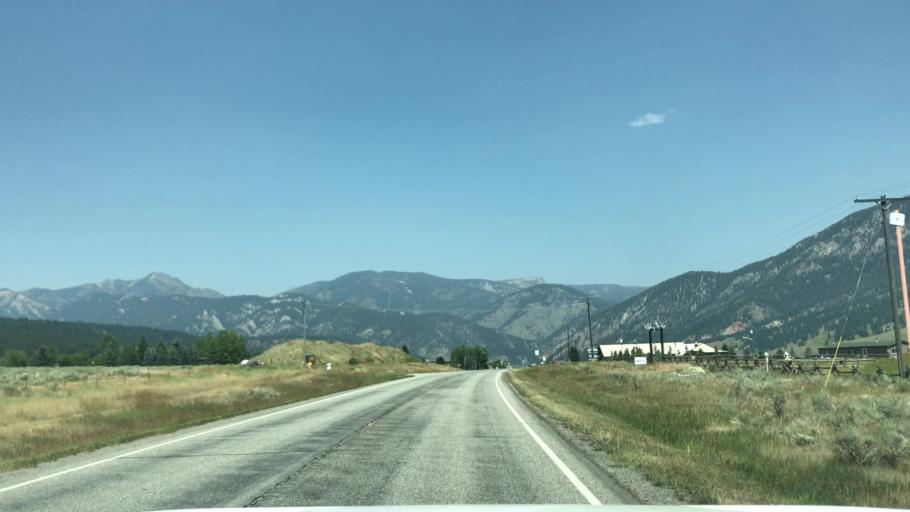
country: US
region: Montana
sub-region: Gallatin County
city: Big Sky
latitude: 45.2216
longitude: -111.2507
